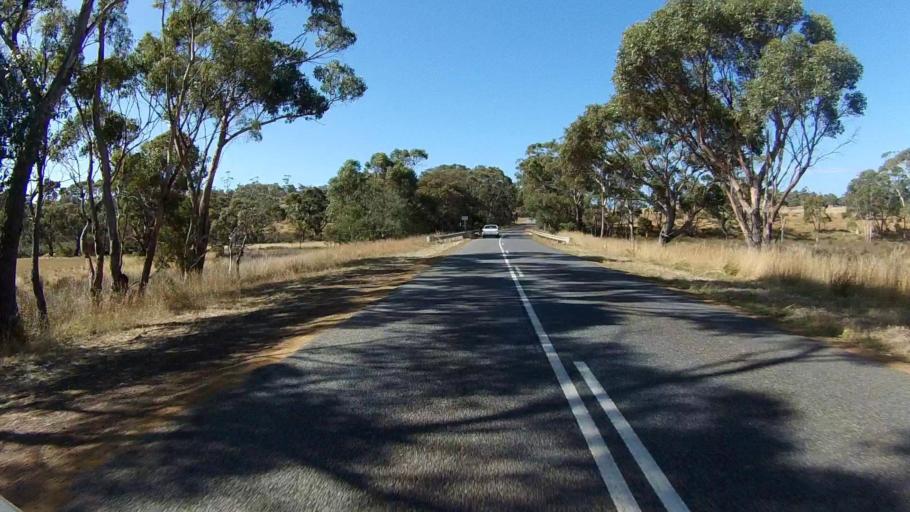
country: AU
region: Tasmania
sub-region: Sorell
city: Sorell
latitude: -42.3058
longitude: 147.9660
